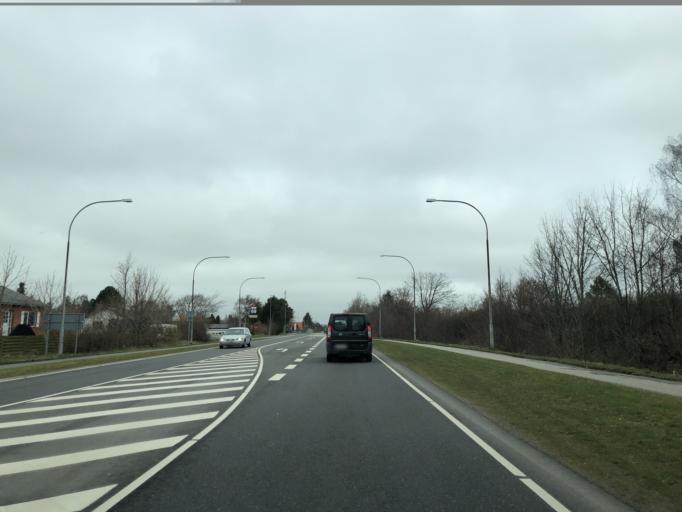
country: DK
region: North Denmark
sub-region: Frederikshavn Kommune
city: Saeby
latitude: 57.3429
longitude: 10.5152
